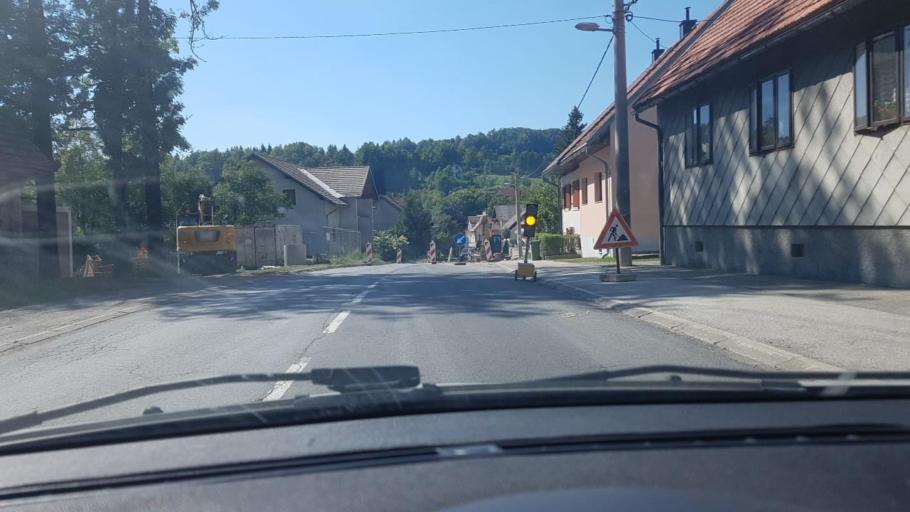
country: HR
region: Primorsko-Goranska
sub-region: Grad Delnice
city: Delnice
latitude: 45.3741
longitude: 14.9212
